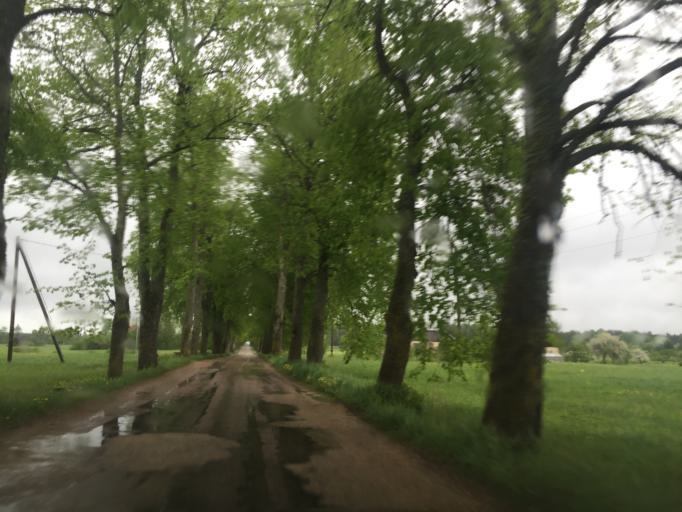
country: LV
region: Ogre
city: Jumprava
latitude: 56.6465
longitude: 24.9227
